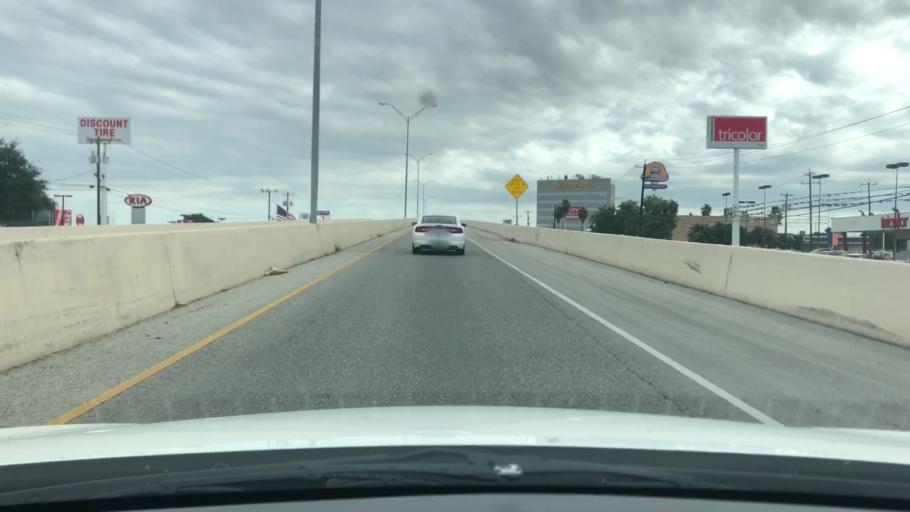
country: US
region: Texas
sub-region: Bexar County
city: Leon Valley
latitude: 29.4876
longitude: -98.6086
